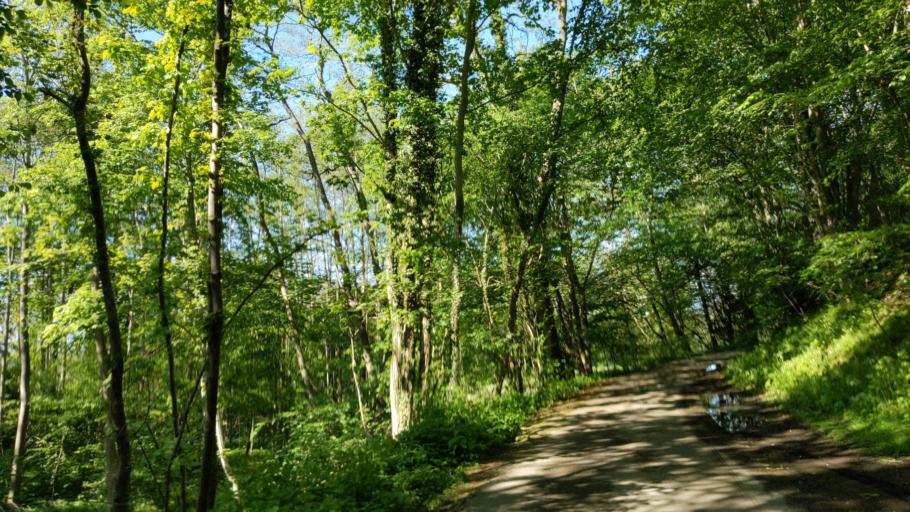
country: DE
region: Schleswig-Holstein
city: Eutin
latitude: 54.1031
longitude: 10.5883
